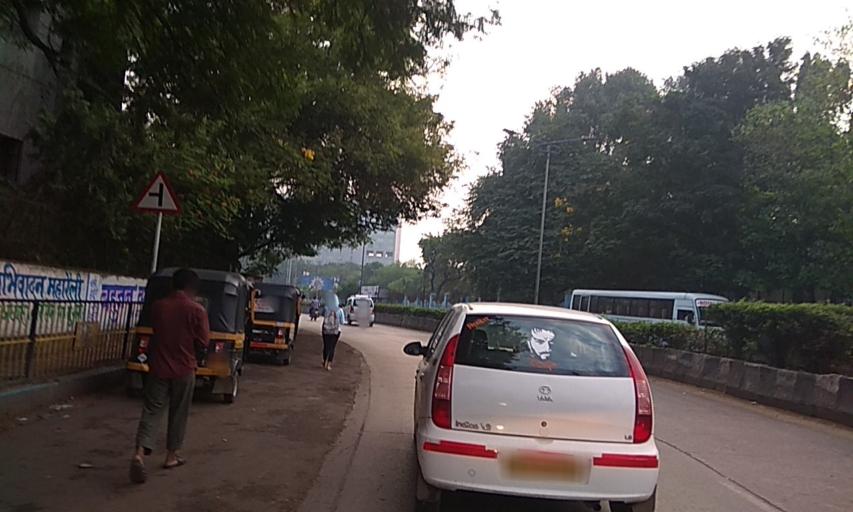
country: IN
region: Maharashtra
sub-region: Pune Division
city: Pune
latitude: 18.5299
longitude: 73.8744
